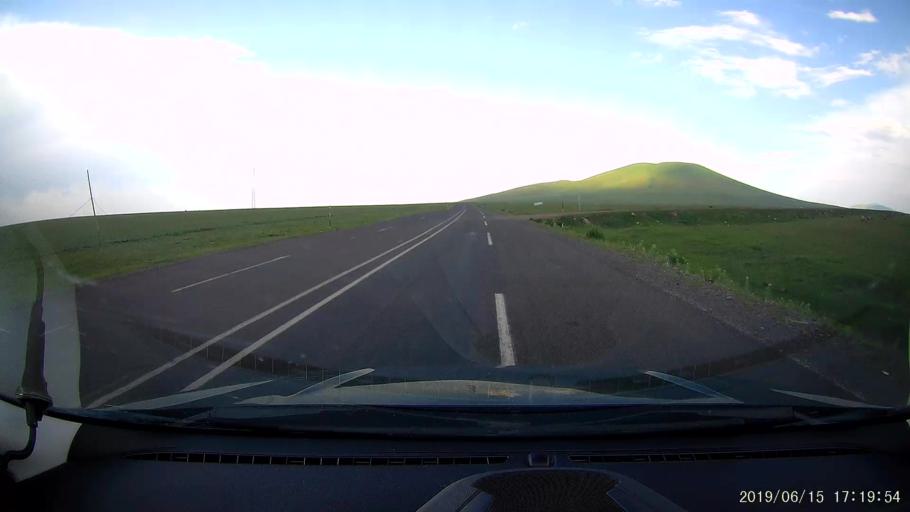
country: TR
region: Kars
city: Kars
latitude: 40.6161
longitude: 43.2888
